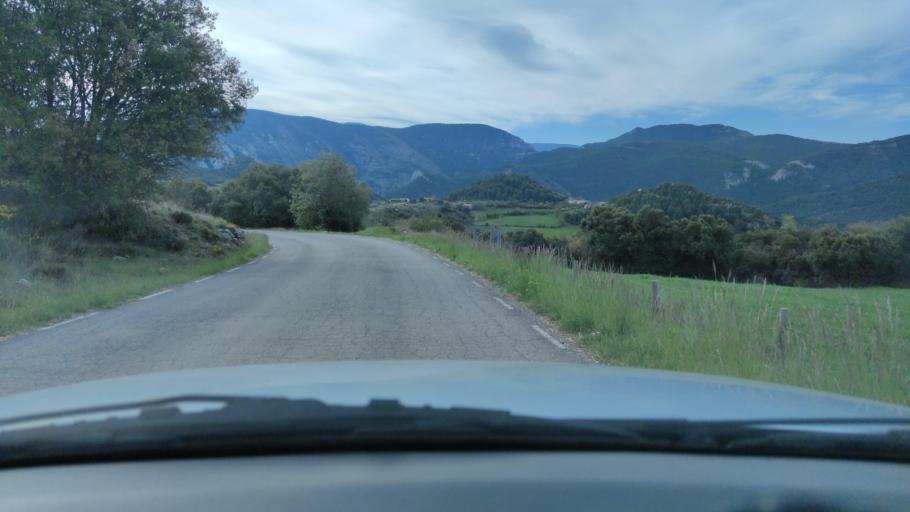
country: ES
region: Catalonia
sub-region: Provincia de Lleida
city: Coll de Nargo
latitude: 42.2376
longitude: 1.3818
